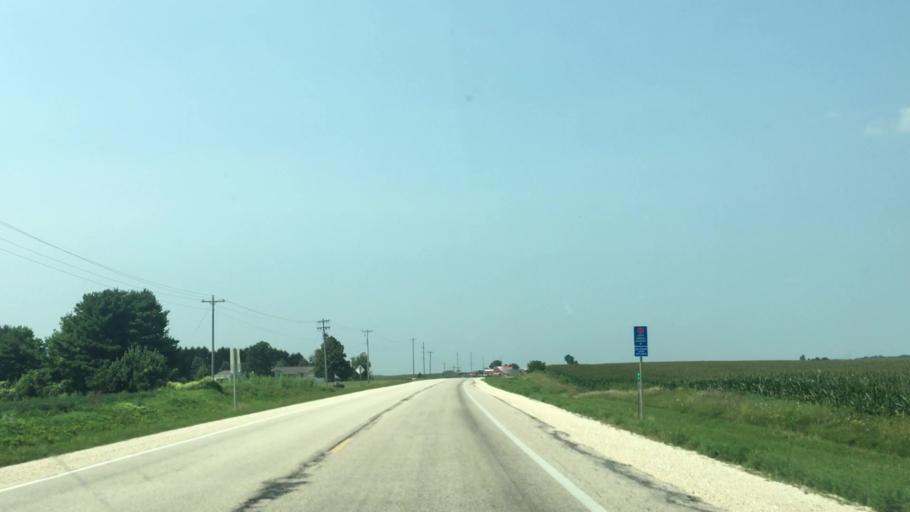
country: US
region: Iowa
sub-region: Fayette County
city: West Union
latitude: 42.9723
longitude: -91.8180
